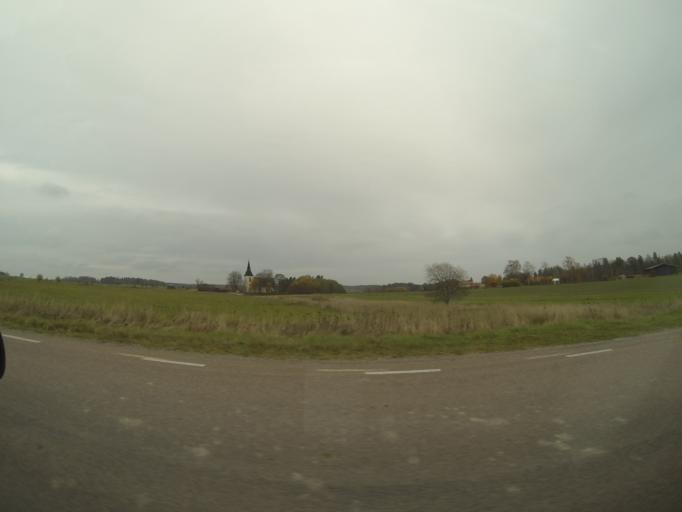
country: SE
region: Vaestmanland
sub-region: Vasteras
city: Vasteras
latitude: 59.6420
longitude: 16.4776
